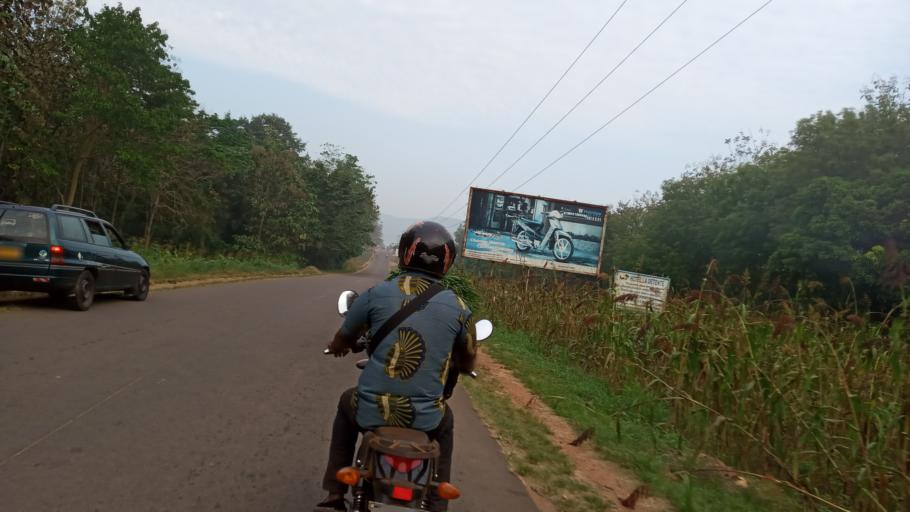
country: TG
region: Plateaux
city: Kpalime
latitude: 6.8877
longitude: 0.6436
